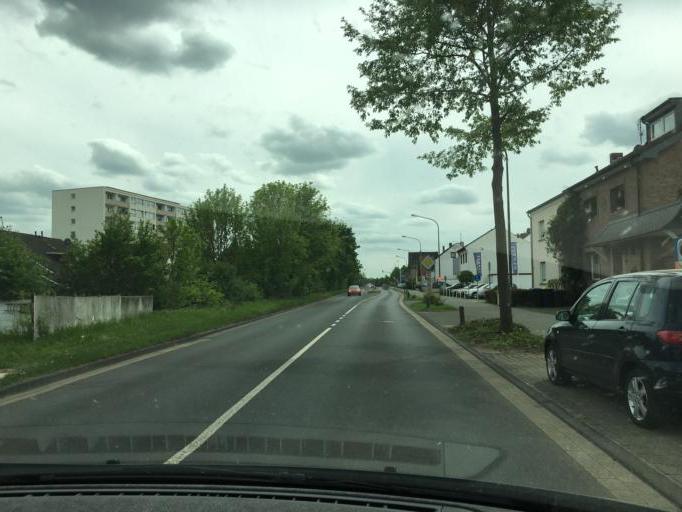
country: DE
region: North Rhine-Westphalia
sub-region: Regierungsbezirk Koln
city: Euskirchen
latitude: 50.6649
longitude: 6.8068
